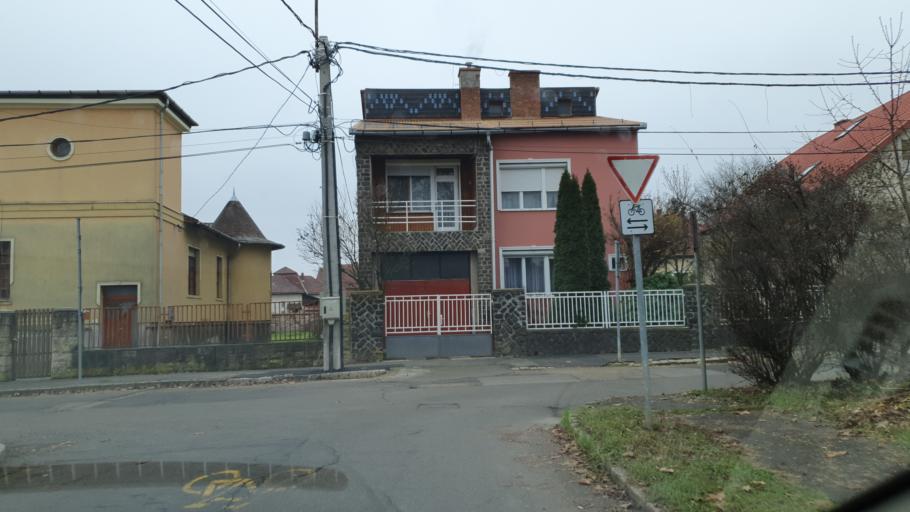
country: HU
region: Borsod-Abauj-Zemplen
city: Miskolc
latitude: 48.1091
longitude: 20.7917
